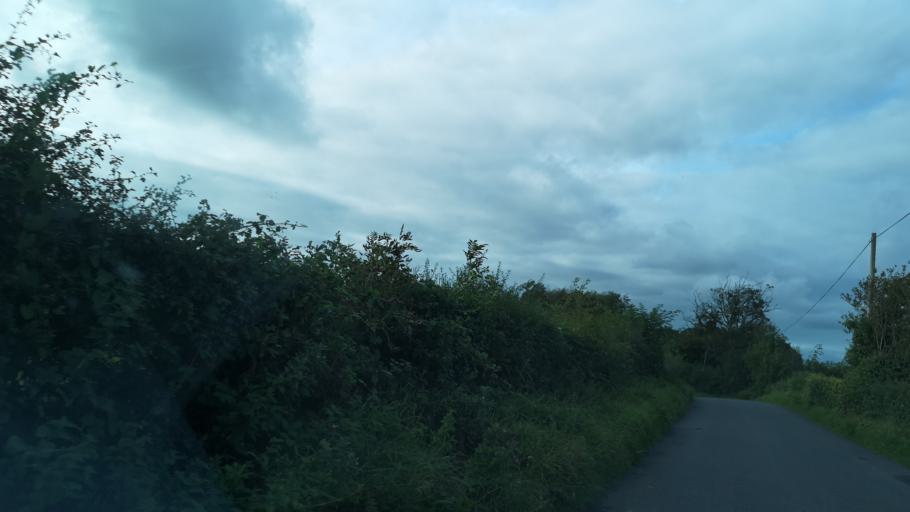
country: IE
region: Connaught
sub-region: County Galway
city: Ballinasloe
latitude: 53.3008
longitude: -8.1012
